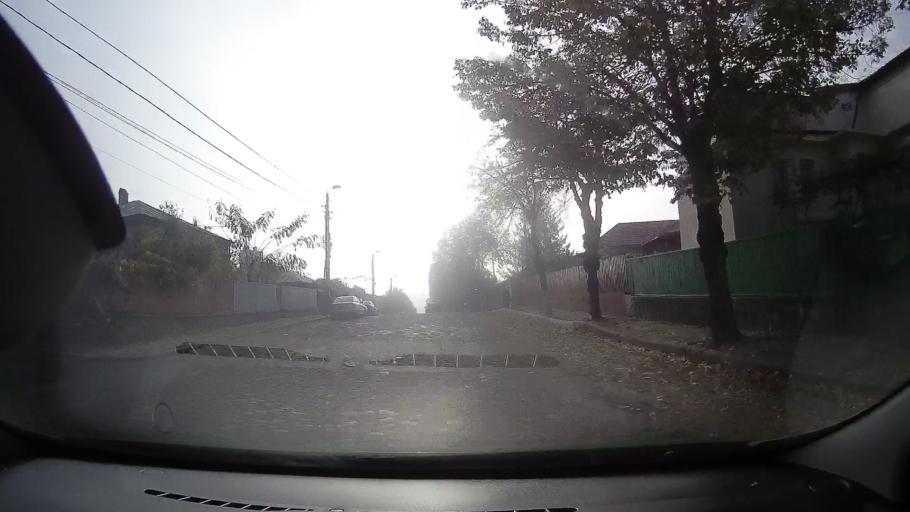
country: RO
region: Tulcea
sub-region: Municipiul Tulcea
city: Tulcea
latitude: 45.1701
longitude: 28.8126
